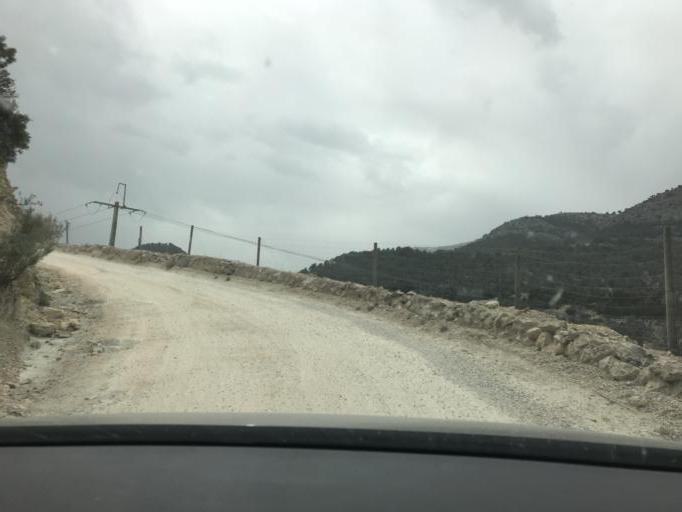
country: ES
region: Andalusia
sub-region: Provincia de Granada
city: Castril
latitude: 37.8317
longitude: -2.7736
